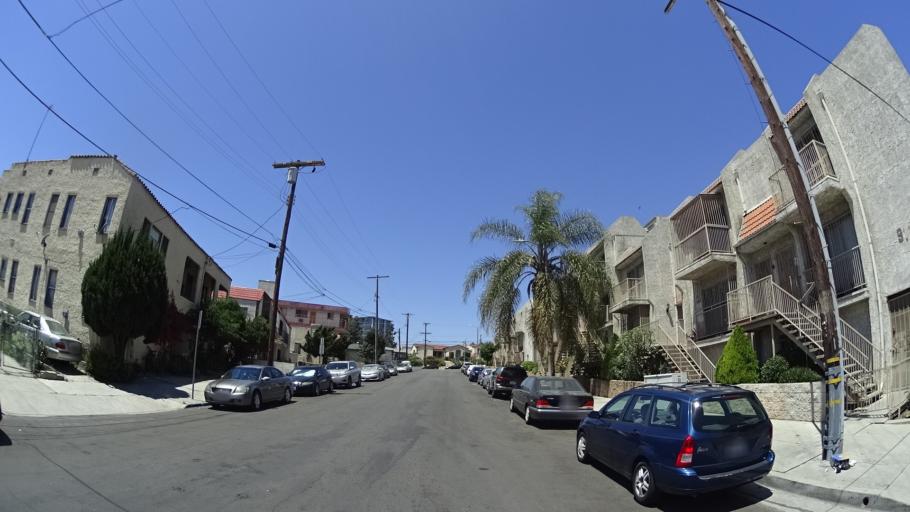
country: US
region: California
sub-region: Los Angeles County
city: Los Angeles
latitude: 34.0655
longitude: -118.2455
